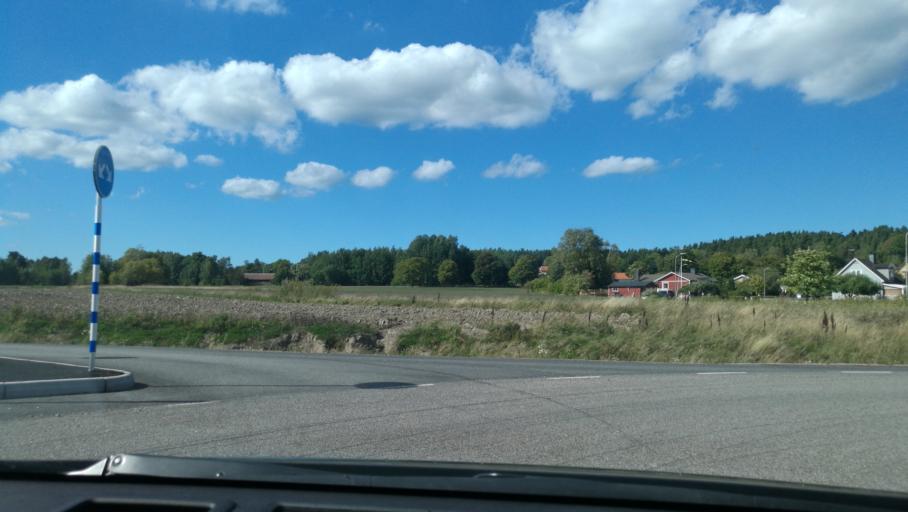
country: SE
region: Vaestra Goetaland
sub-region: Mariestads Kommun
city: Mariestad
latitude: 58.6789
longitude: 13.8154
